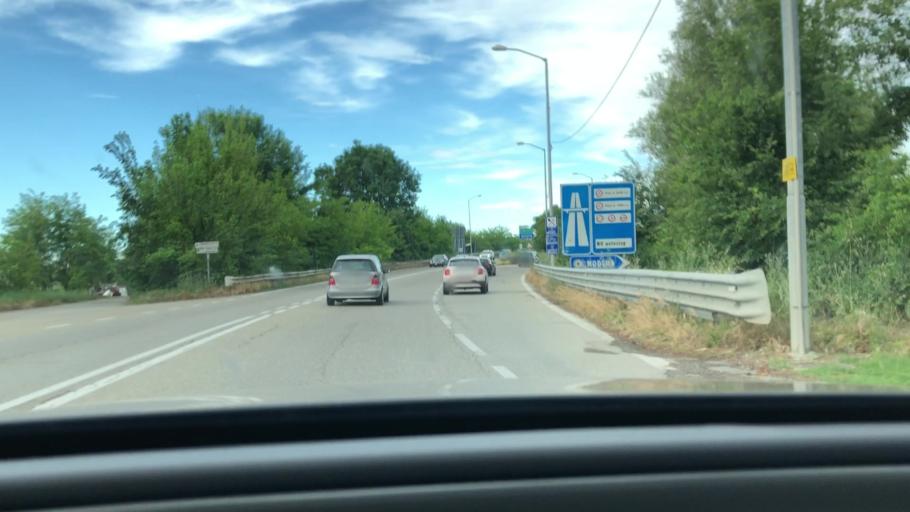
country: IT
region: Emilia-Romagna
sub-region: Provincia di Modena
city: Montale
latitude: 44.6016
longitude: 10.9312
